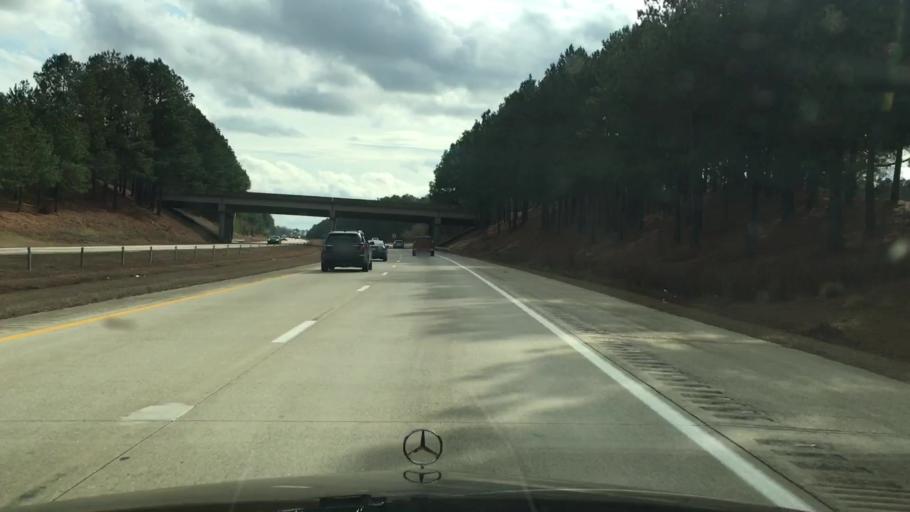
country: US
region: North Carolina
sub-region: Johnston County
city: Benson
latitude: 35.4242
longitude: -78.5308
